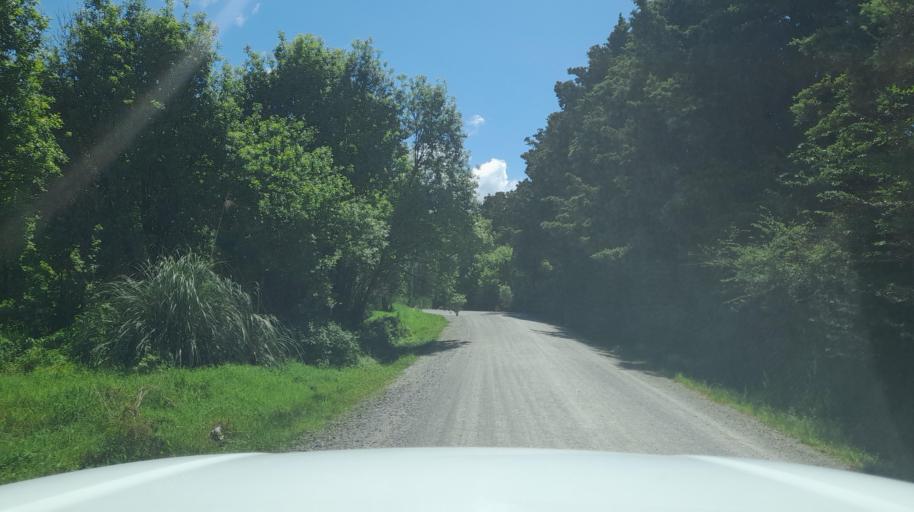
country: NZ
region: Northland
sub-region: Far North District
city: Taipa
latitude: -35.1207
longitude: 173.4063
